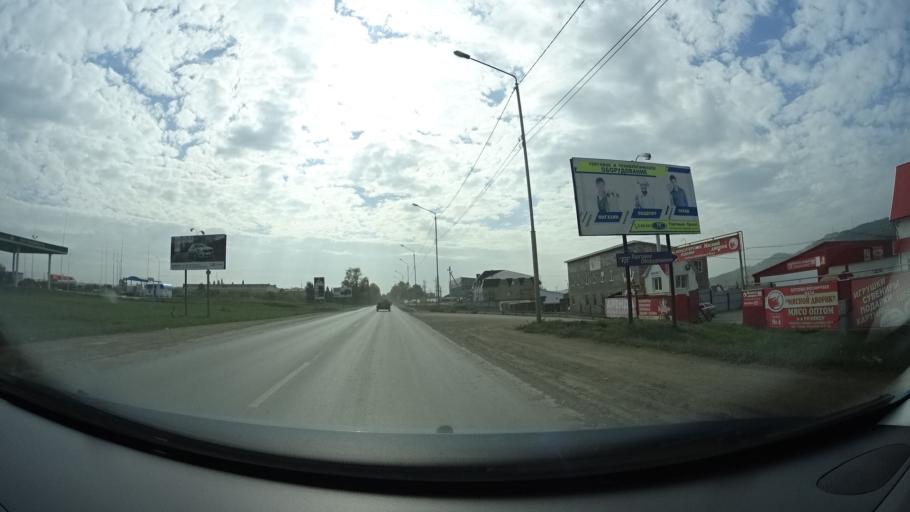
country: RU
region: Bashkortostan
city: Oktyabr'skiy
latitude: 54.5015
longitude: 53.5058
